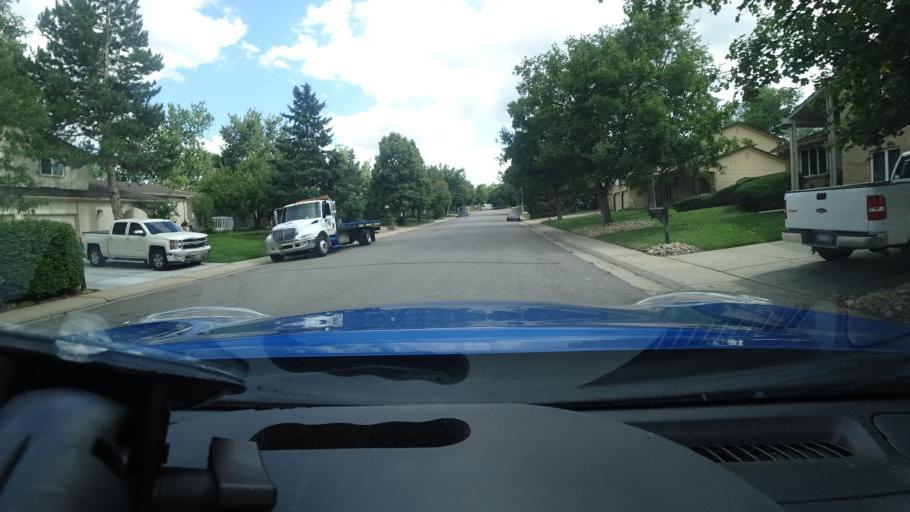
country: US
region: Colorado
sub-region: Adams County
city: Aurora
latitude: 39.6856
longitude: -104.8534
